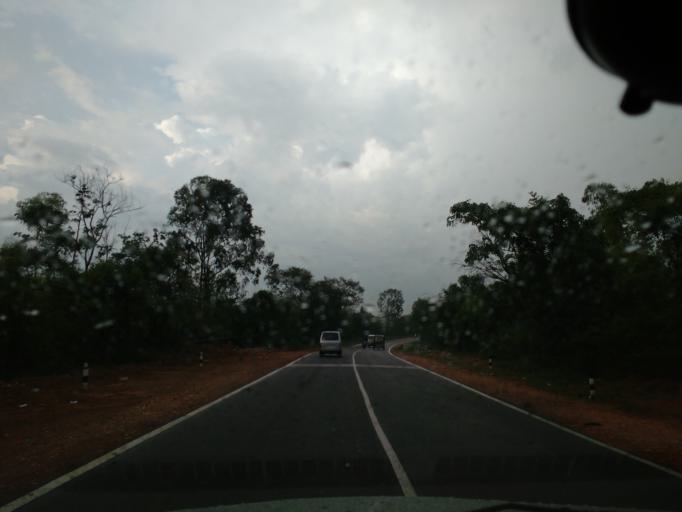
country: IN
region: Karnataka
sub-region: Tumkur
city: Tiptur
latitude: 13.2956
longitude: 76.5833
